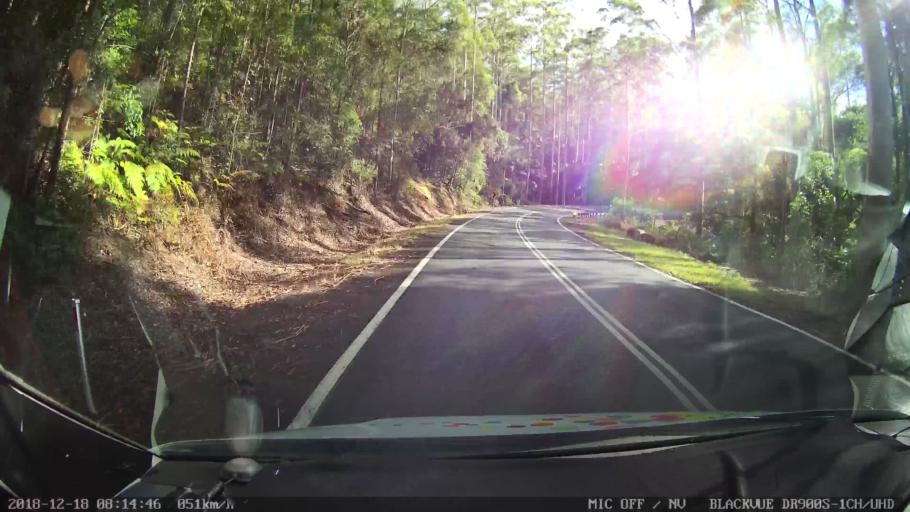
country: AU
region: New South Wales
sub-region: Kyogle
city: Kyogle
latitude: -28.3354
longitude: 152.6834
